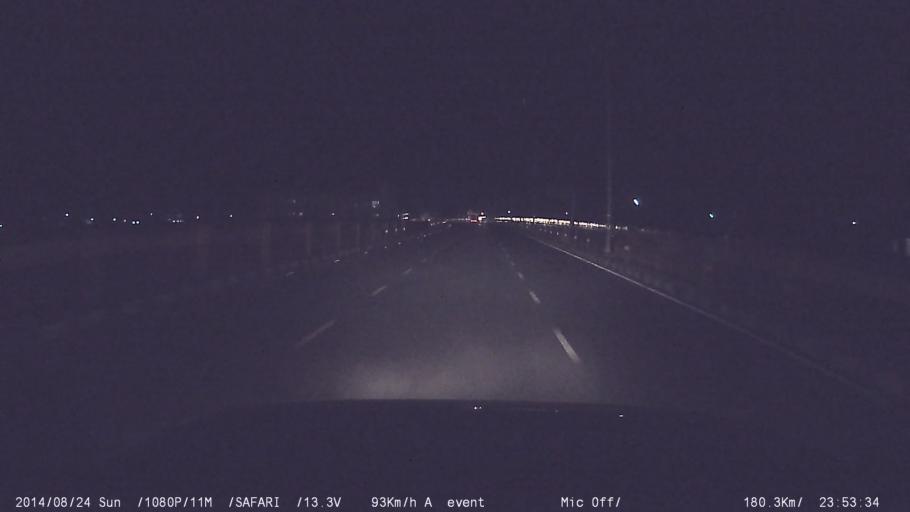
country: IN
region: Tamil Nadu
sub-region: Krishnagiri
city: Krishnagiri
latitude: 12.5324
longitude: 78.2430
